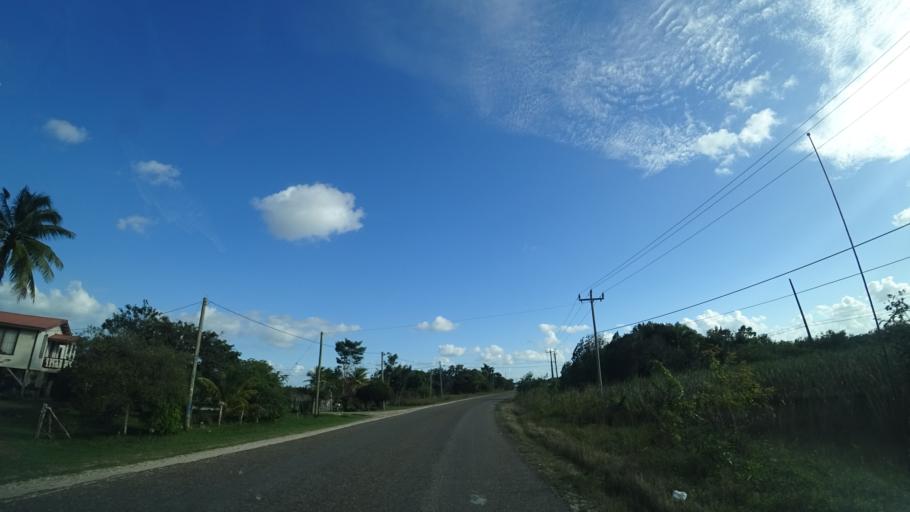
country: BZ
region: Belize
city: Belize City
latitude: 17.5832
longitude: -88.3450
